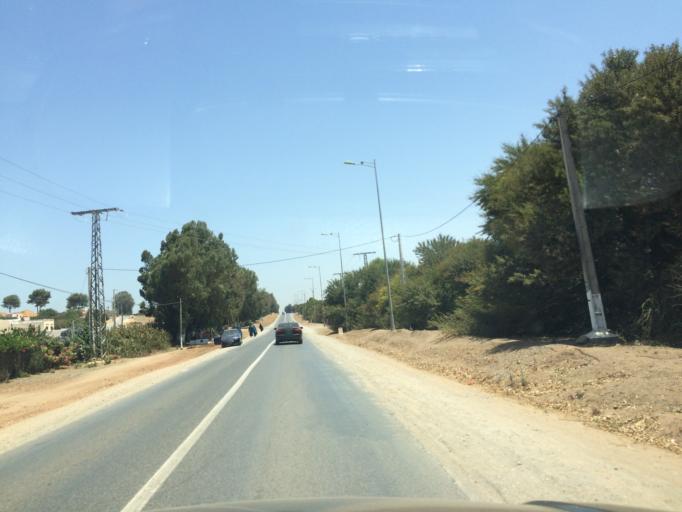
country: MA
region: Rabat-Sale-Zemmour-Zaer
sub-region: Skhirate-Temara
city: Temara
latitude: 33.8724
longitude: -6.8524
